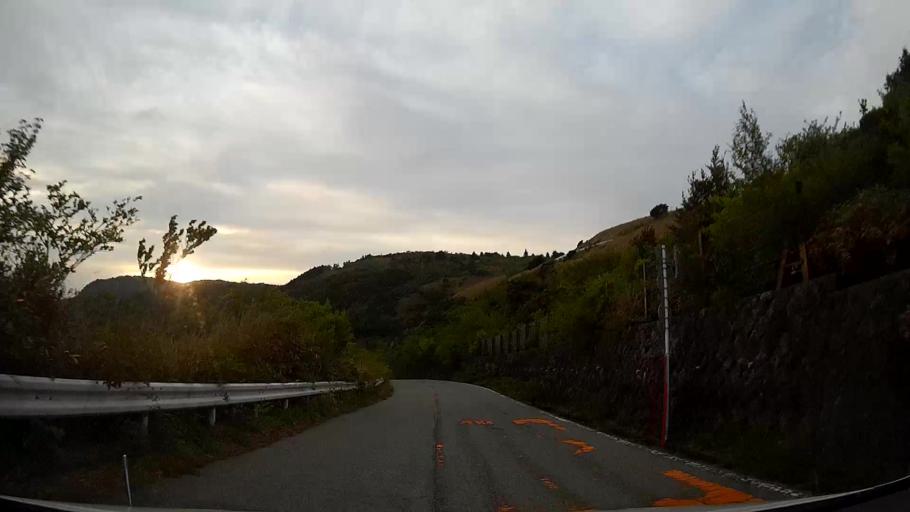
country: JP
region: Kanagawa
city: Yugawara
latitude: 35.1799
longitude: 139.0642
